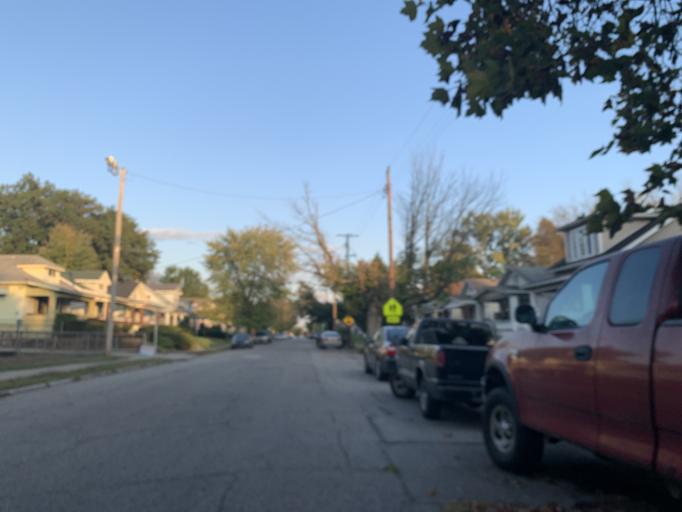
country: US
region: Indiana
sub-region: Floyd County
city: New Albany
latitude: 38.2574
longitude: -85.8235
